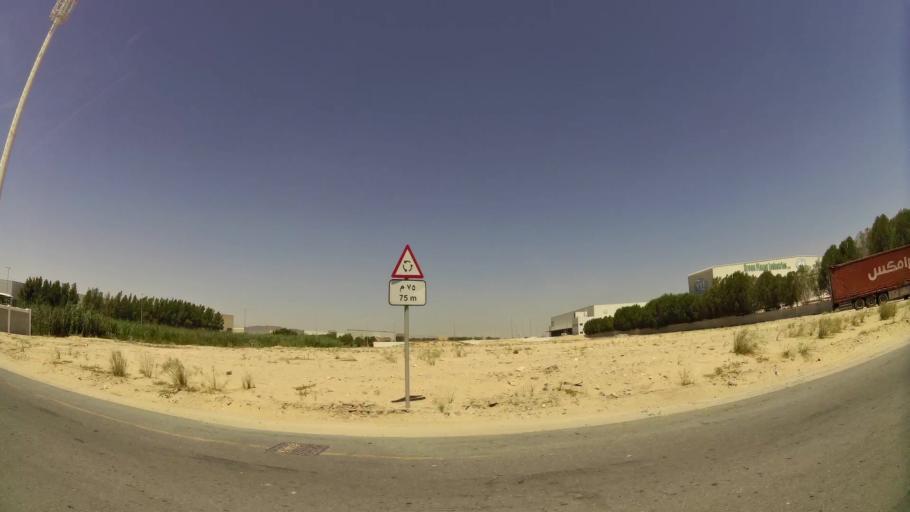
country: AE
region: Dubai
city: Dubai
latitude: 24.9868
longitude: 55.1919
